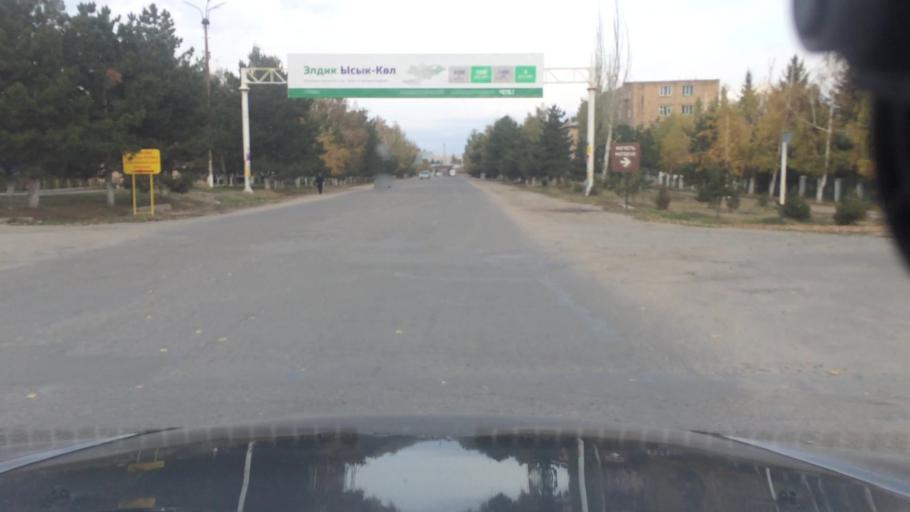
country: KG
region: Ysyk-Koel
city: Karakol
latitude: 42.4966
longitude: 78.3910
